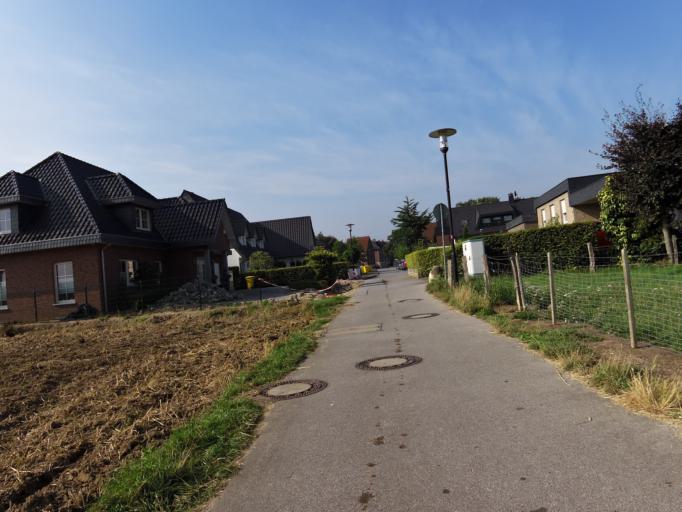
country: DE
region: North Rhine-Westphalia
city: Geilenkirchen
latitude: 50.9666
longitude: 6.1300
